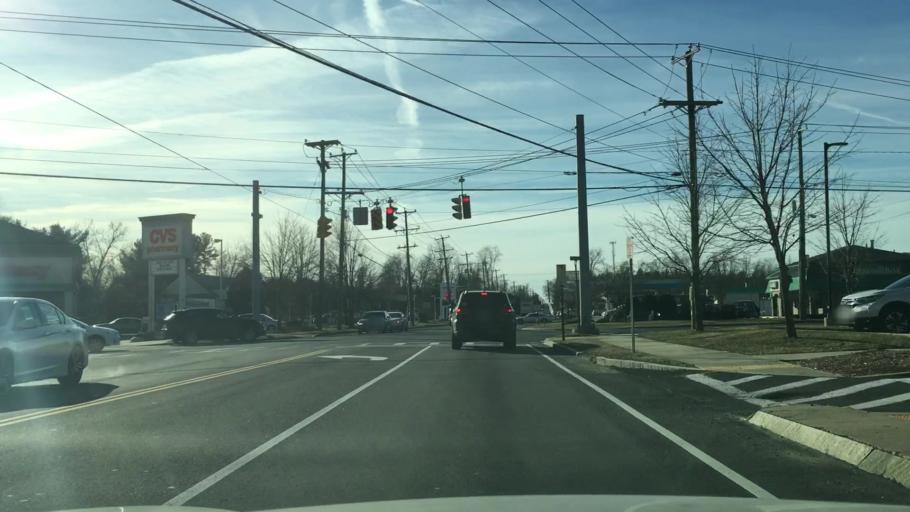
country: US
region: Massachusetts
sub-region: Hampden County
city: Agawam
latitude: 42.0624
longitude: -72.6320
